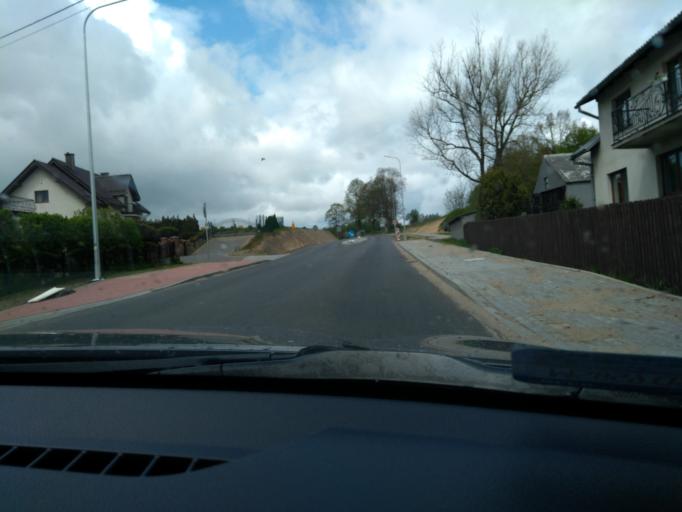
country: PL
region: Pomeranian Voivodeship
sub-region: Powiat kartuski
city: Chmielno
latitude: 54.3422
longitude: 18.0537
